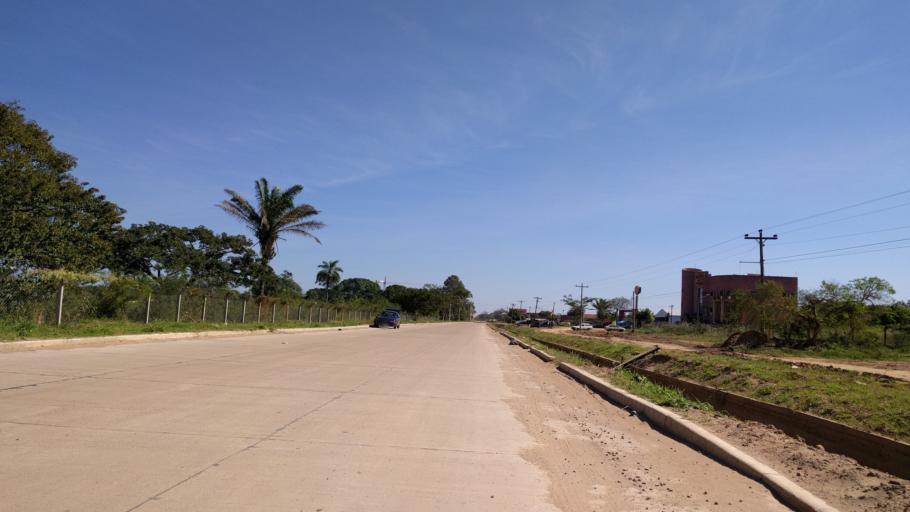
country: BO
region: Santa Cruz
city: Santa Cruz de la Sierra
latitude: -17.8464
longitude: -63.2268
